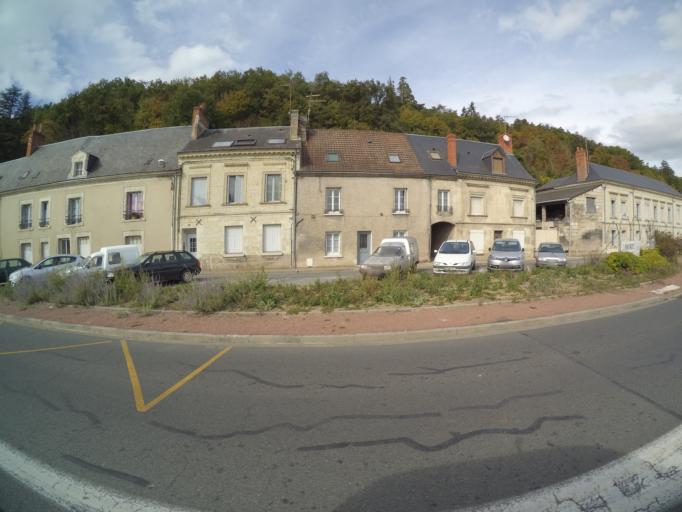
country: FR
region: Centre
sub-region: Departement d'Indre-et-Loire
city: Langeais
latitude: 47.3211
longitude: 0.3998
